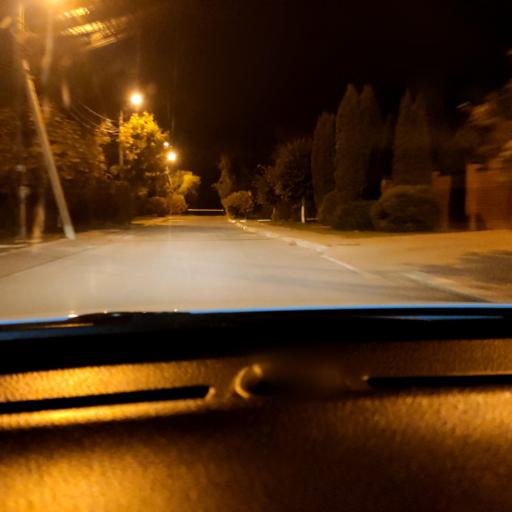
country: RU
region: Voronezj
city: Voronezh
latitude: 51.7234
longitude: 39.2259
